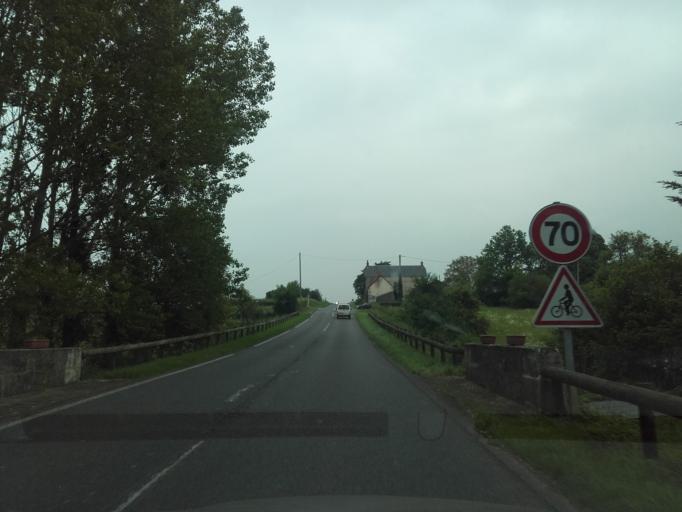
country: FR
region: Centre
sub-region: Departement d'Indre-et-Loire
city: Neuvy-le-Roi
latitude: 47.6555
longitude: 0.6490
